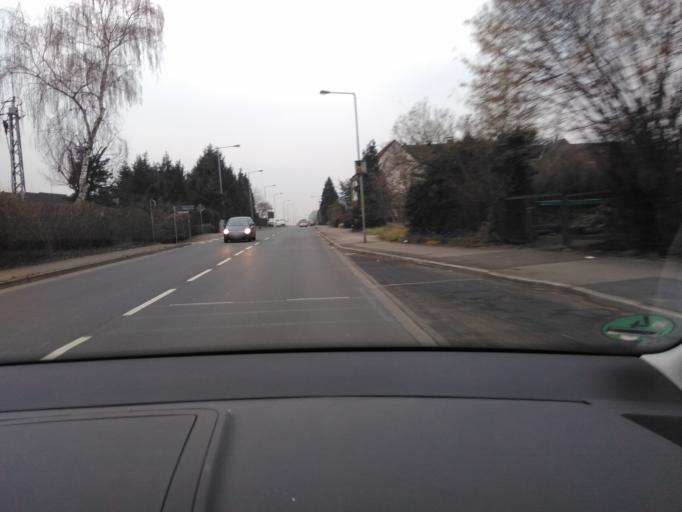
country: DE
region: North Rhine-Westphalia
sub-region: Regierungsbezirk Koln
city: Odenthal
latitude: 51.0514
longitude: 7.0889
